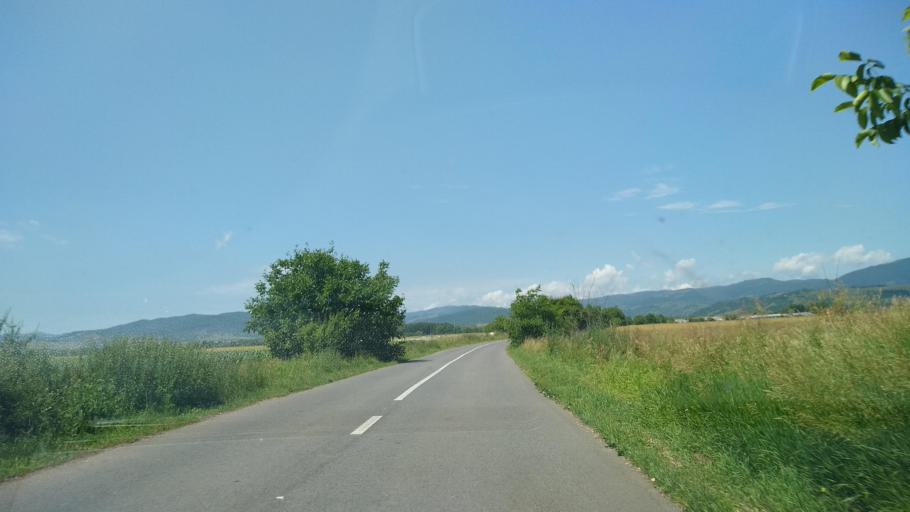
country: RO
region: Hunedoara
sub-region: Comuna Totesti
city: Totesti
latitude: 45.5742
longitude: 22.8655
